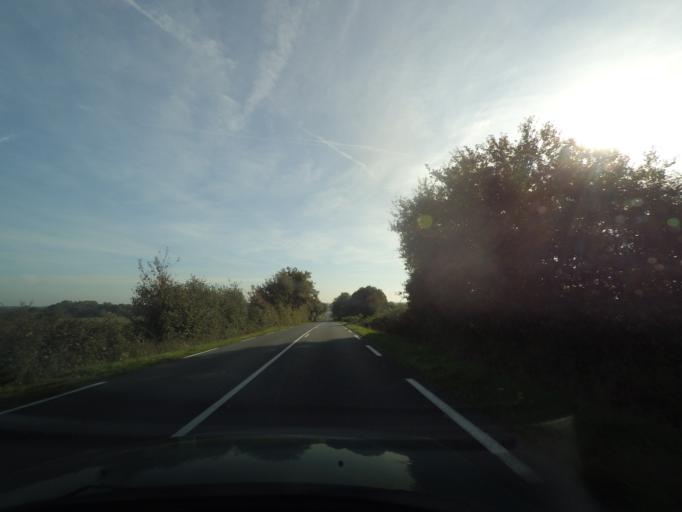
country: FR
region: Pays de la Loire
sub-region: Departement de la Vendee
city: Montaigu
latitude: 46.9819
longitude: -1.2822
